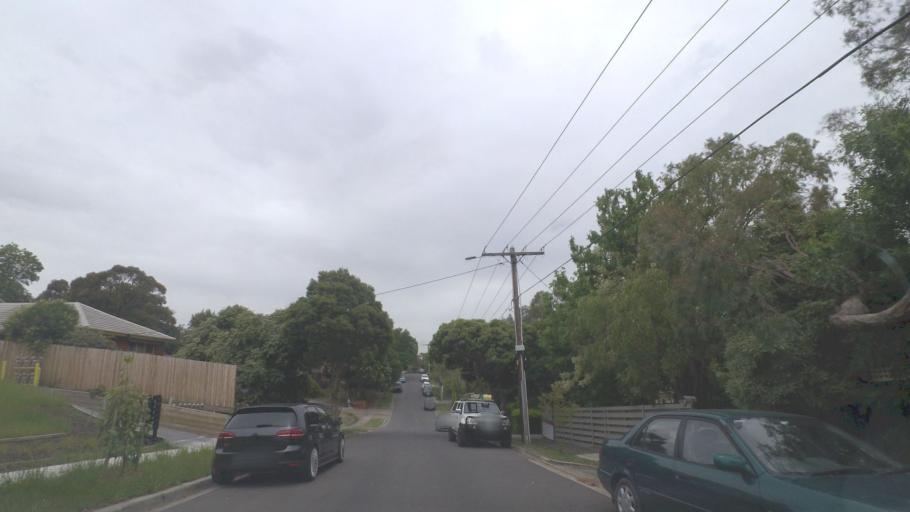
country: AU
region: Victoria
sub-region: Maroondah
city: Croydon North
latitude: -37.7870
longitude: 145.3061
